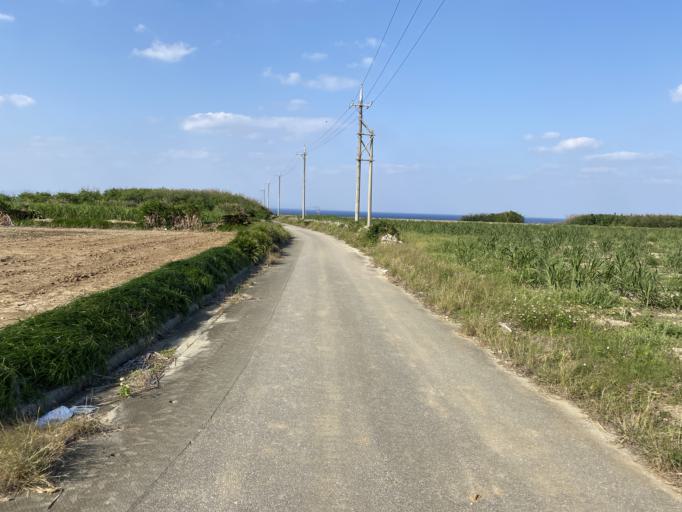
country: JP
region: Okinawa
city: Ishigaki
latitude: 24.0662
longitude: 123.7896
